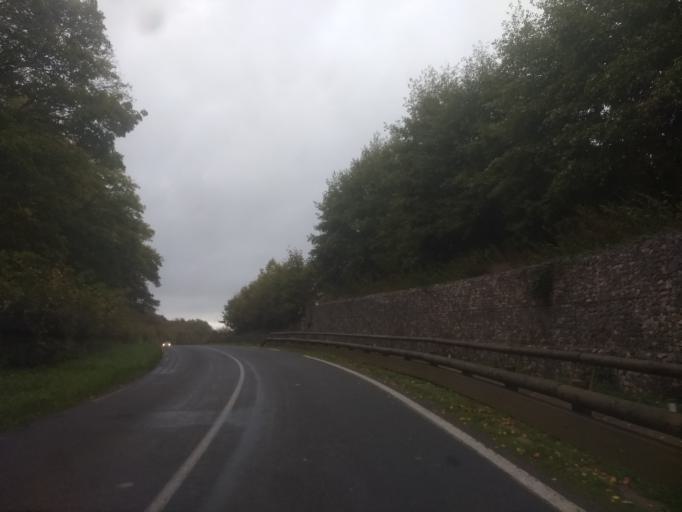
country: FR
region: Nord-Pas-de-Calais
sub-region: Departement du Pas-de-Calais
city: Wissant
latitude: 50.8956
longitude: 1.6865
